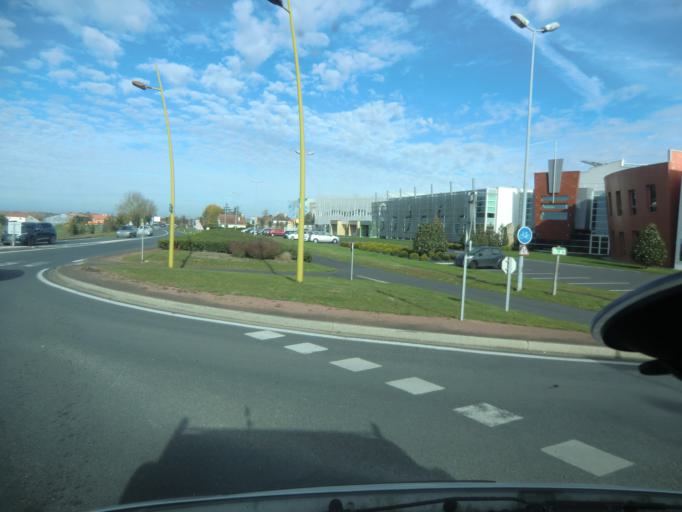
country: FR
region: Pays de la Loire
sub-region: Departement de la Vendee
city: Montaigu
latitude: 46.9616
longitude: -1.3062
